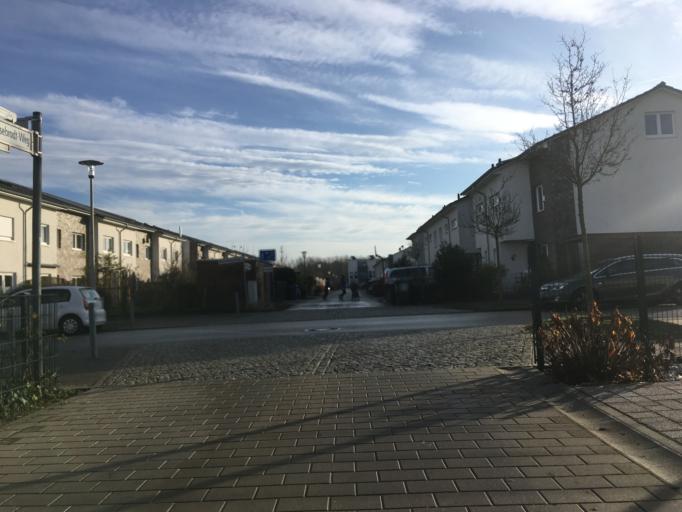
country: DE
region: Berlin
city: Karlshorst
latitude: 52.4754
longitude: 13.5350
